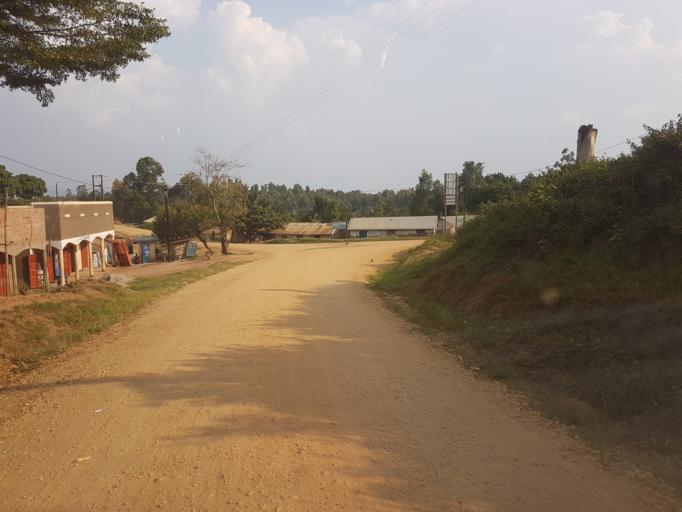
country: UG
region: Western Region
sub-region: Rukungiri District
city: Rukungiri
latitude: -0.6472
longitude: 29.8450
